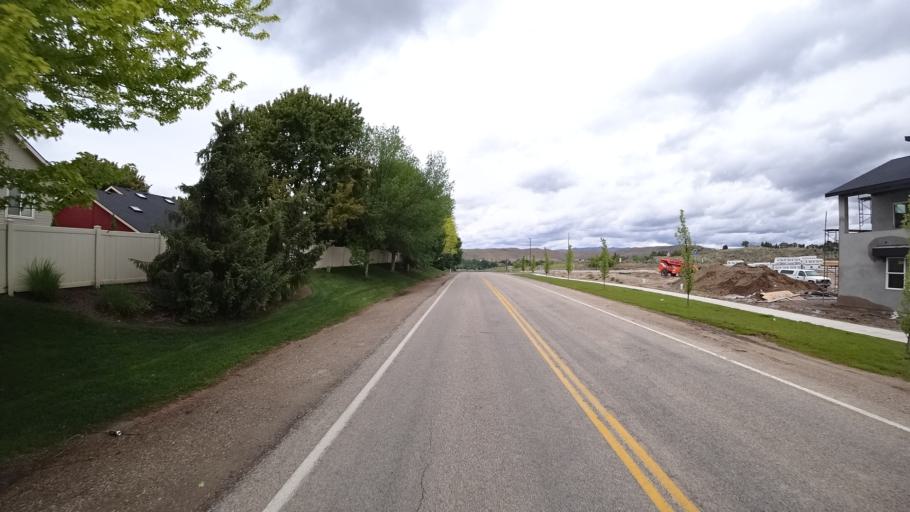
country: US
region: Idaho
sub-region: Ada County
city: Eagle
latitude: 43.7144
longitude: -116.3169
